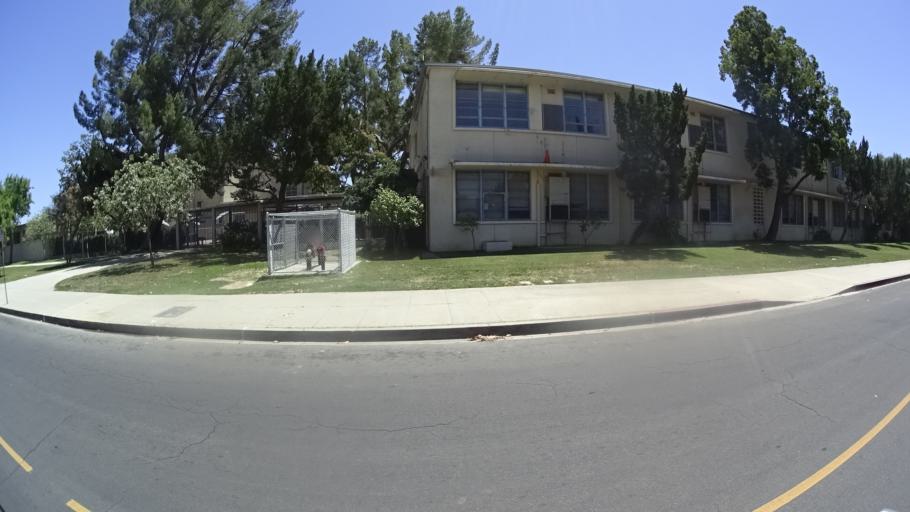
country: US
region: California
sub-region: Los Angeles County
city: Northridge
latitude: 34.1903
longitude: -118.5298
